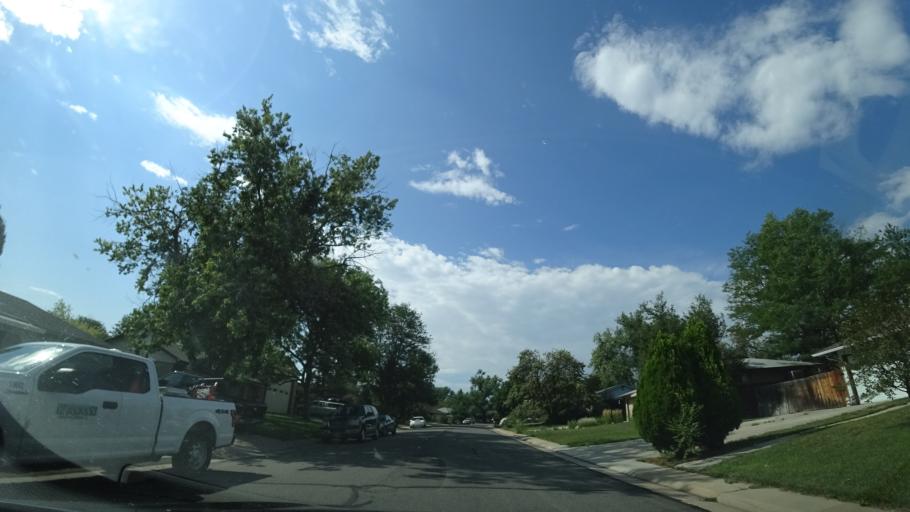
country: US
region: Colorado
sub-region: Jefferson County
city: Lakewood
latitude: 39.7180
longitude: -105.0556
